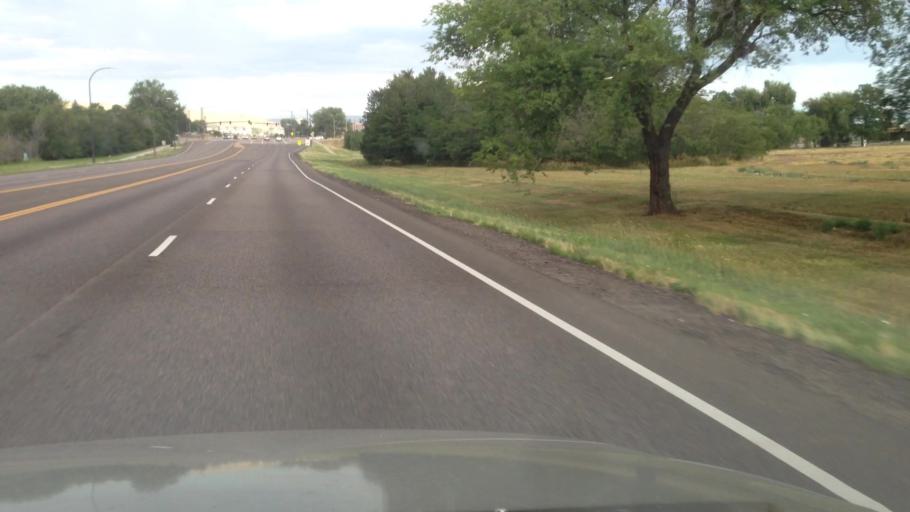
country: US
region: Colorado
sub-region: Jefferson County
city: Lakewood
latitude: 39.7108
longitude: -105.1050
